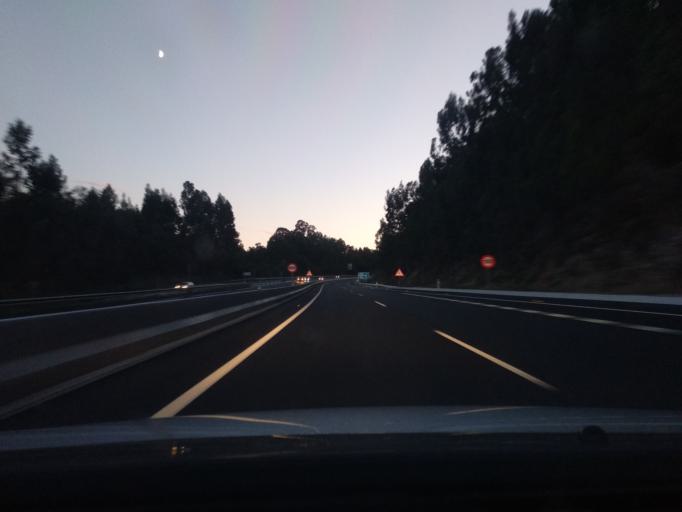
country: ES
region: Galicia
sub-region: Provincia de Pontevedra
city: Moana
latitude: 42.3024
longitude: -8.7445
